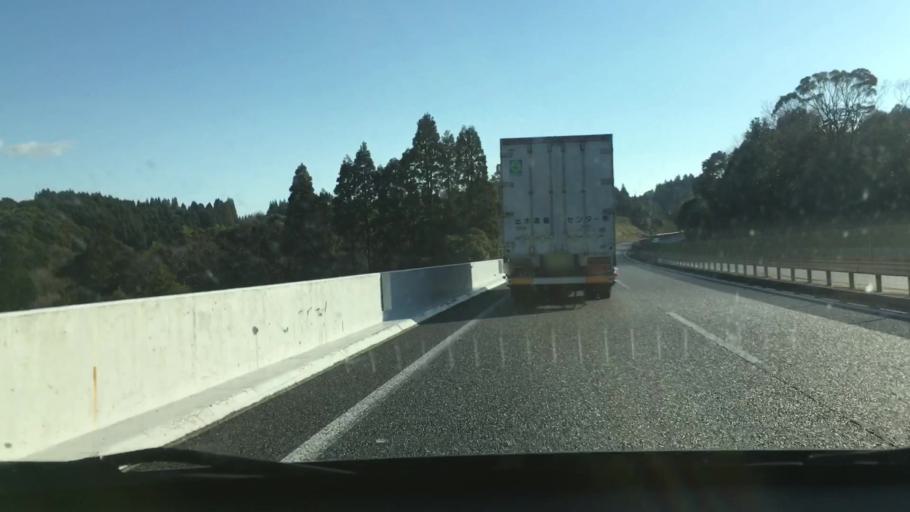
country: JP
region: Kagoshima
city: Kajiki
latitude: 31.8776
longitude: 130.6951
